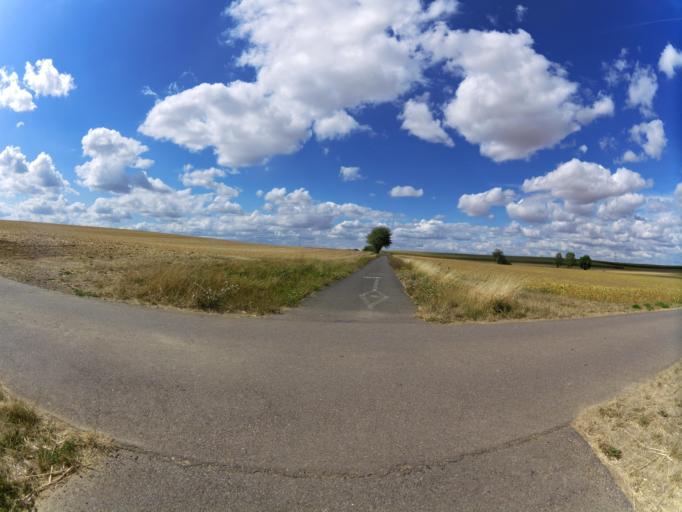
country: DE
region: Bavaria
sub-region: Regierungsbezirk Unterfranken
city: Aub
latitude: 49.5608
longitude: 10.0518
